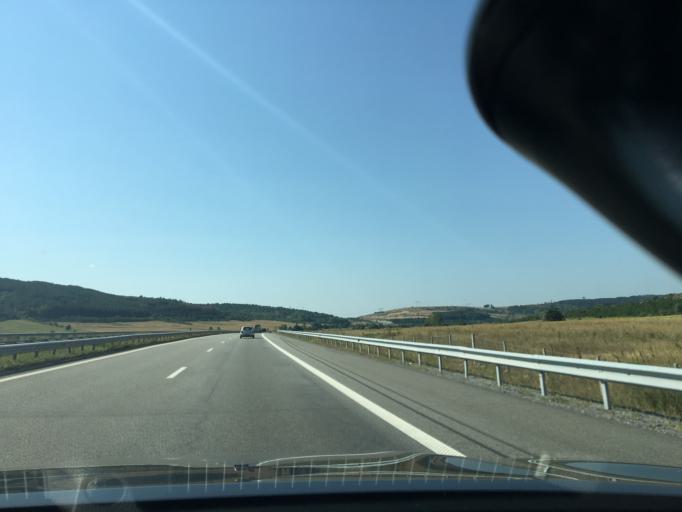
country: BG
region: Kyustendil
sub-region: Obshtina Bobovdol
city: Bobovdol
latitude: 42.3989
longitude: 23.1204
